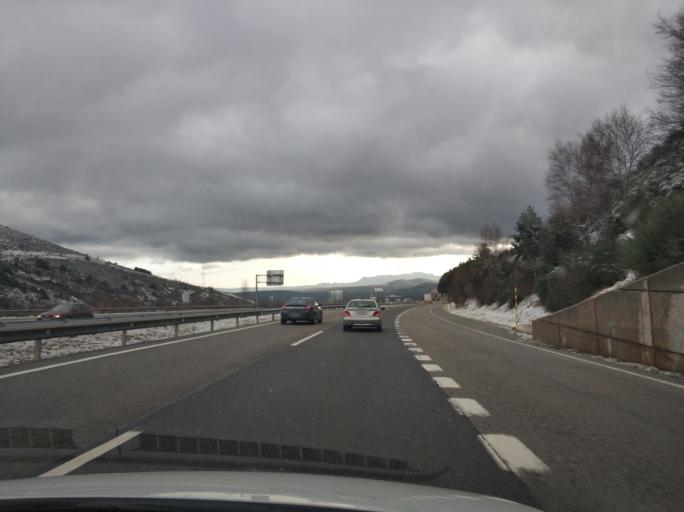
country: ES
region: Madrid
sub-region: Provincia de Madrid
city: Somosierra
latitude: 41.1190
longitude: -3.5865
